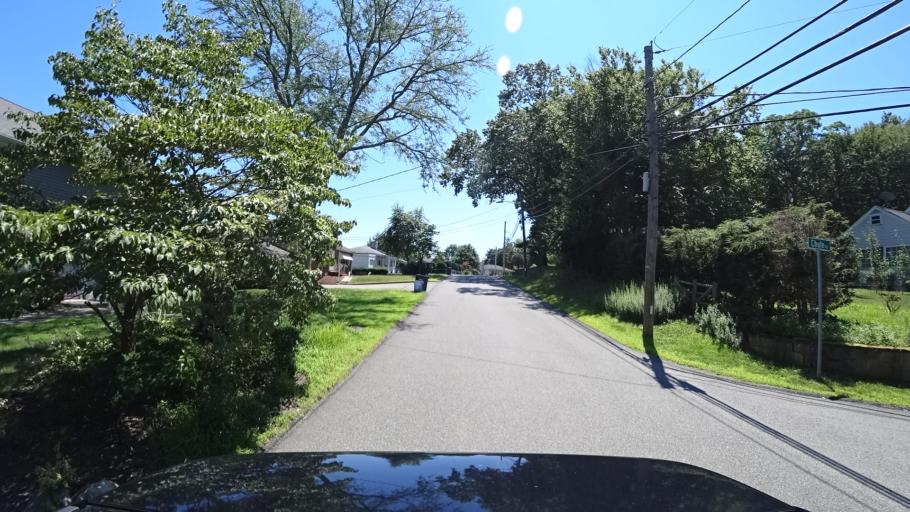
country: US
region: Massachusetts
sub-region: Norfolk County
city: Dedham
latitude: 42.2370
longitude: -71.1836
